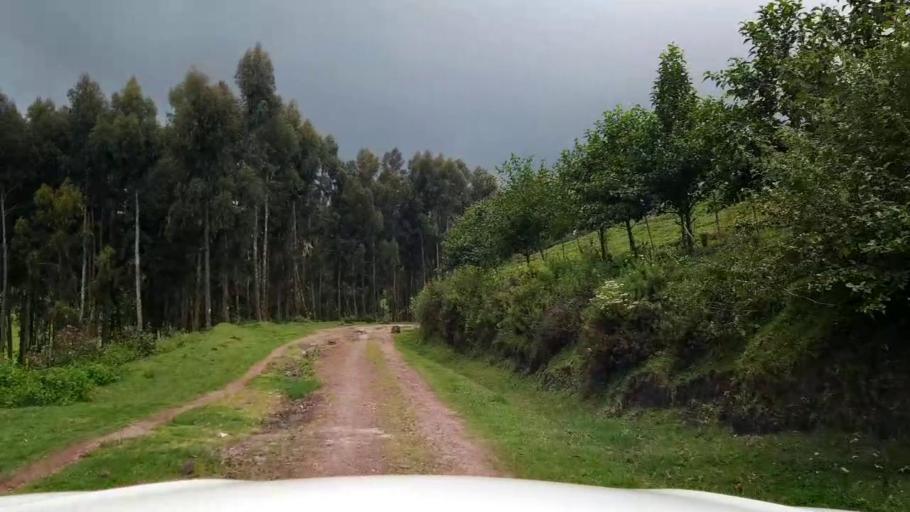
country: RW
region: Western Province
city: Gisenyi
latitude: -1.6884
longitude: 29.4231
